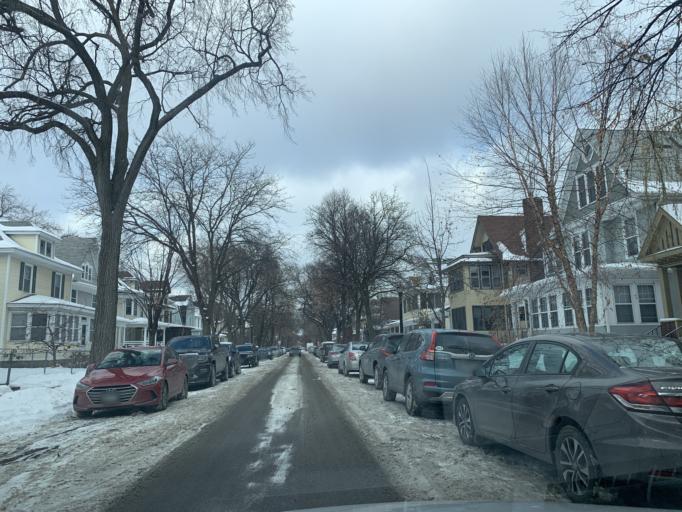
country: US
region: Minnesota
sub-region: Hennepin County
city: Minneapolis
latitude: 44.9524
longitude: -93.2957
